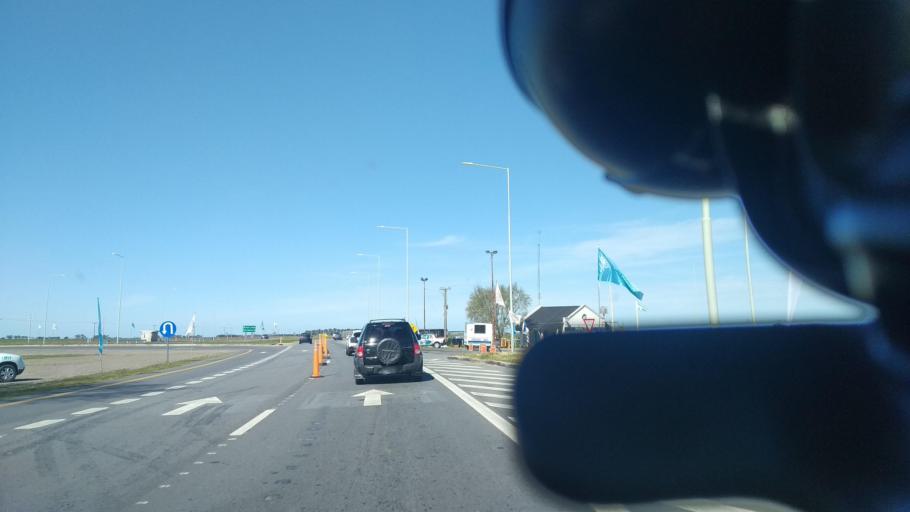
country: AR
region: Buenos Aires
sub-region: Partido de General Lavalle
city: General Lavalle
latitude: -36.4311
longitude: -56.9154
